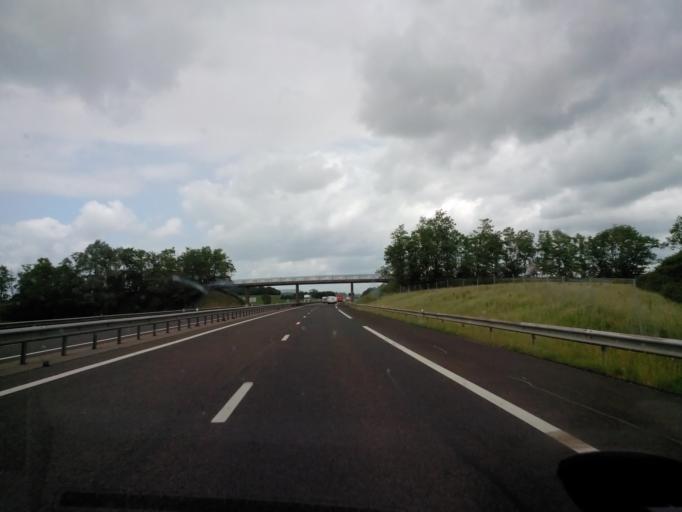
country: FR
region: Lorraine
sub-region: Departement de Meurthe-et-Moselle
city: Blenod-les-Toul
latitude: 48.6049
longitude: 5.8857
